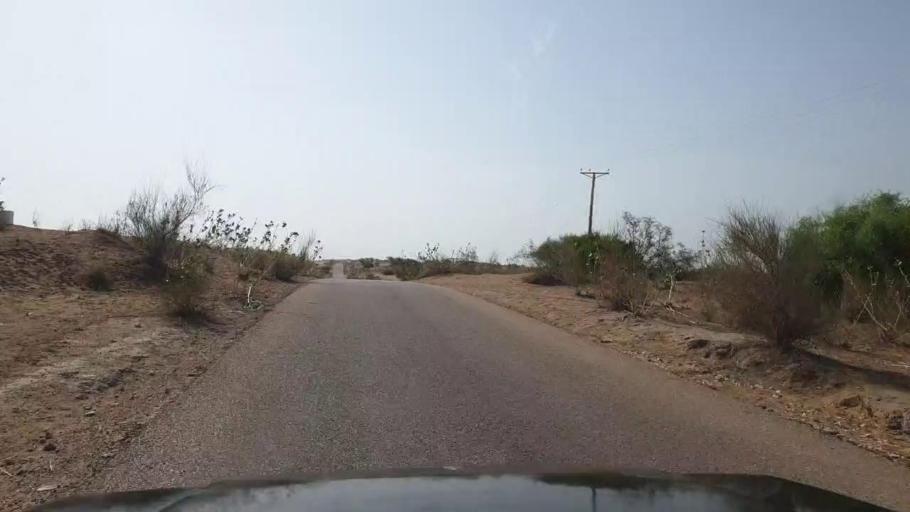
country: PK
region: Sindh
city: Mithi
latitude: 24.9769
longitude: 70.0025
